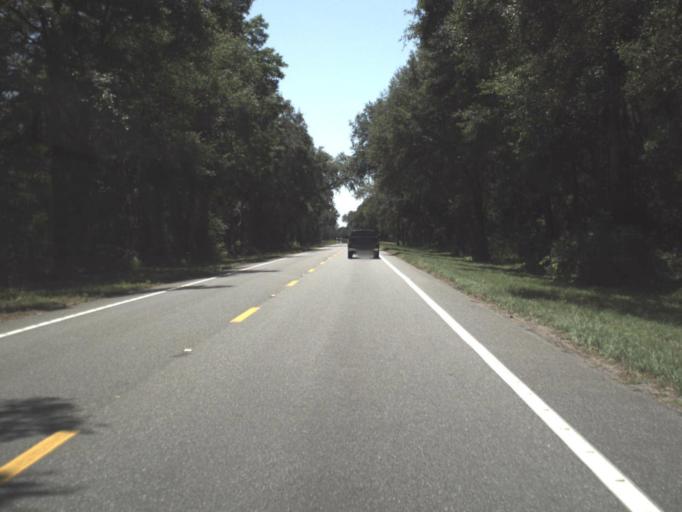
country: US
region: Florida
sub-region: Lafayette County
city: Mayo
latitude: 30.1293
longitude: -83.3153
